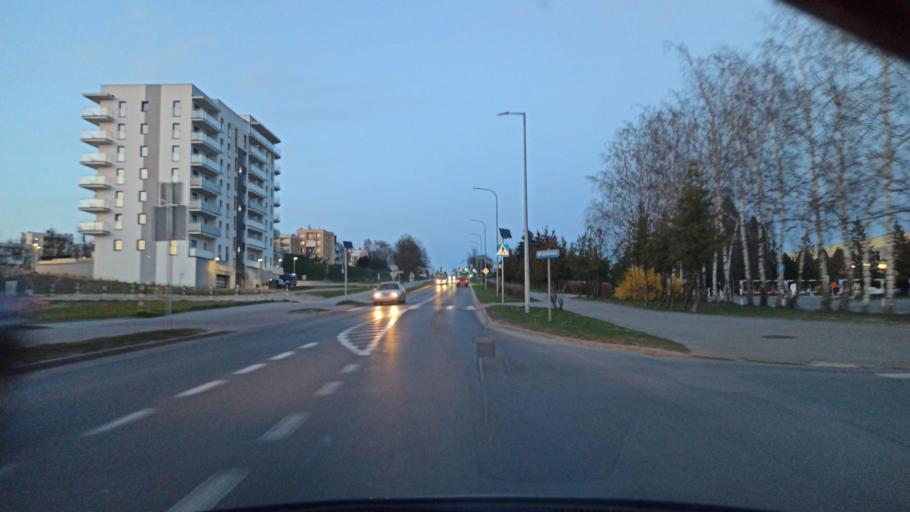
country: PL
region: Warmian-Masurian Voivodeship
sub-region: Powiat elblaski
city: Elblag
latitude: 54.1793
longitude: 19.4272
